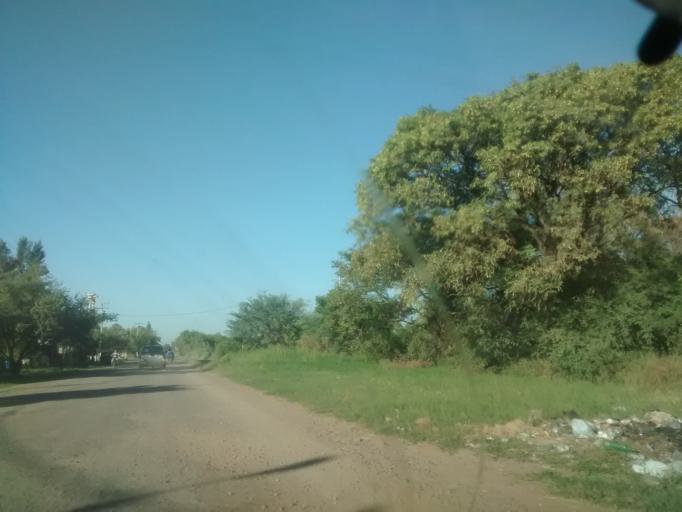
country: AR
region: Chaco
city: Resistencia
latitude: -27.4589
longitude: -59.0238
